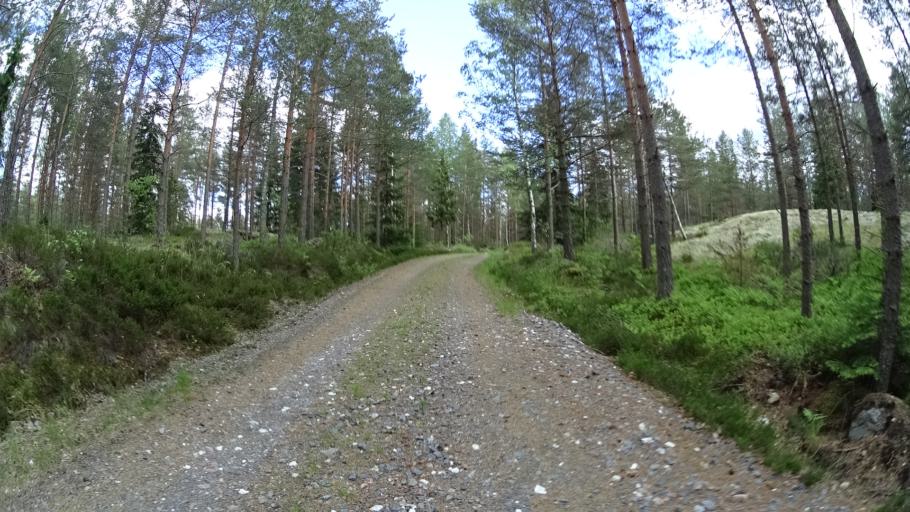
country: FI
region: Varsinais-Suomi
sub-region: Salo
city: Kisko
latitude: 60.1839
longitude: 23.5525
